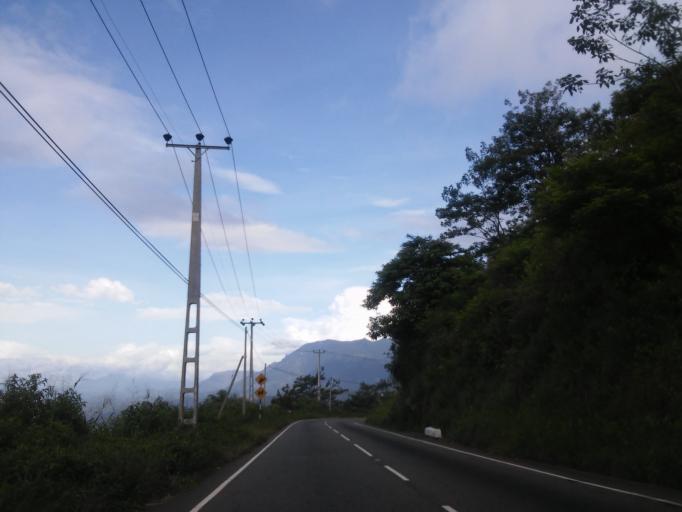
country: LK
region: Uva
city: Haputale
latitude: 6.7608
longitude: 80.9354
